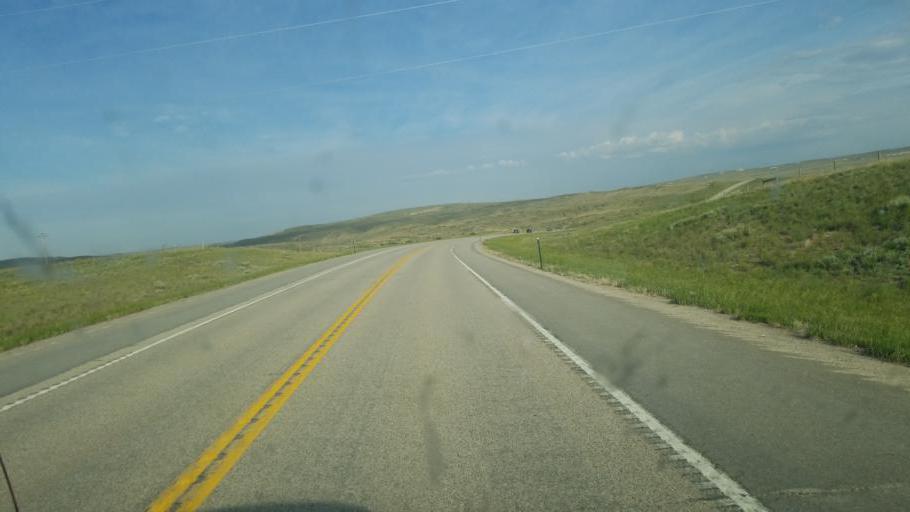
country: US
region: Wyoming
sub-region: Natrona County
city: Mills
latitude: 43.0337
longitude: -107.0122
